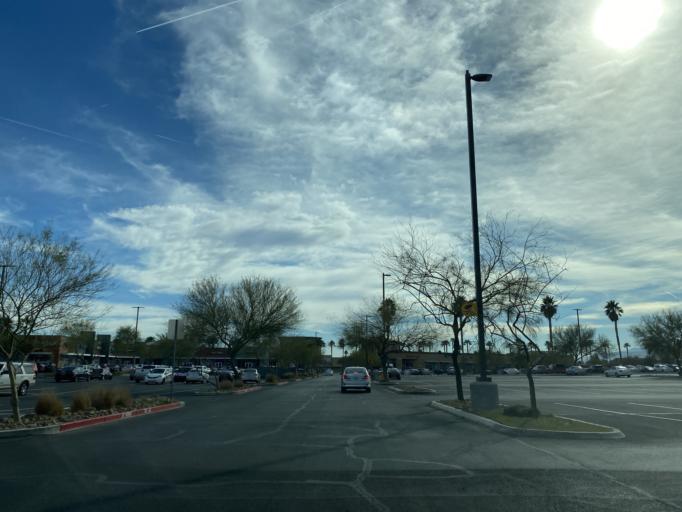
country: US
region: Nevada
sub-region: Clark County
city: Las Vegas
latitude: 36.2726
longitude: -115.2684
